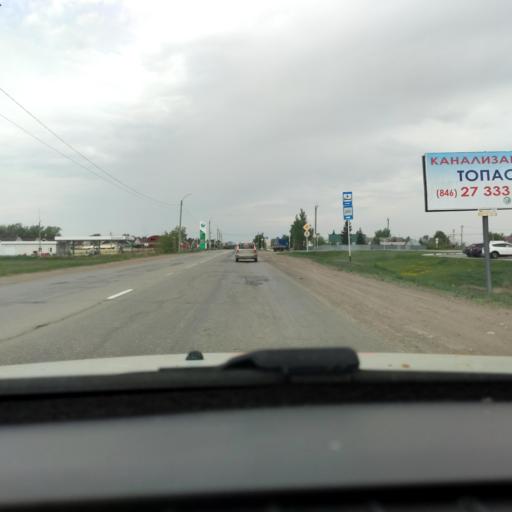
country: RU
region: Samara
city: Krasnyy Yar
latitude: 53.4860
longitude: 50.3896
